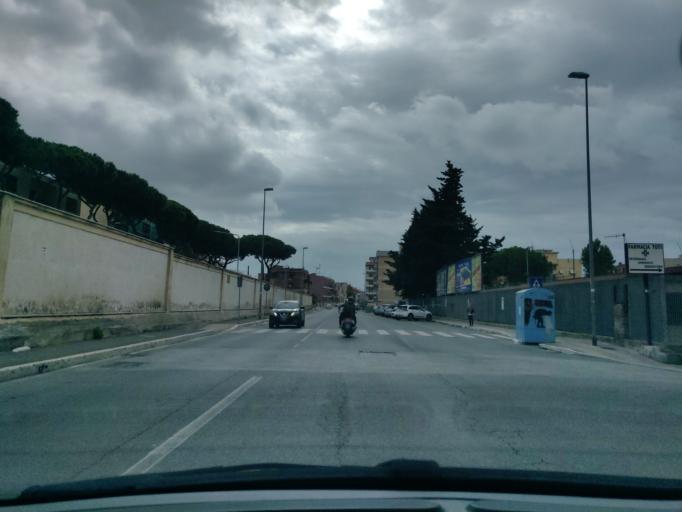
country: IT
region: Latium
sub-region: Citta metropolitana di Roma Capitale
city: Civitavecchia
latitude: 42.0977
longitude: 11.8013
